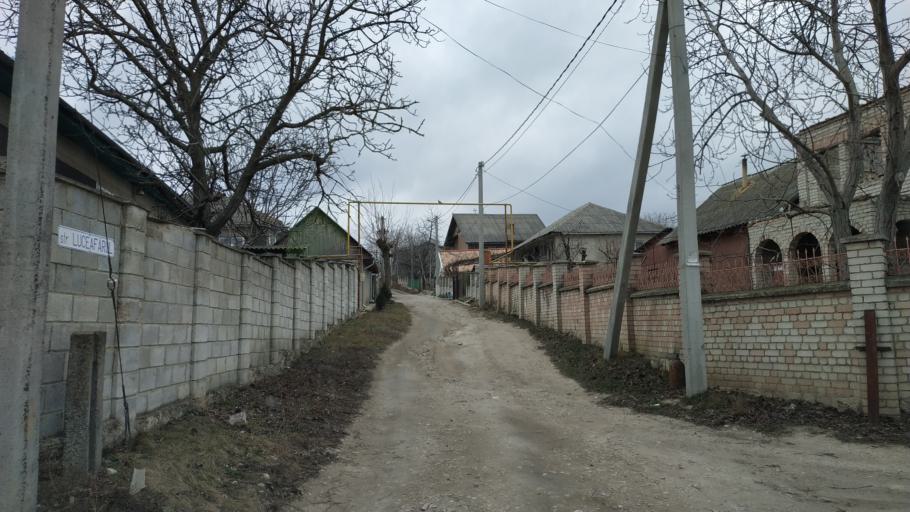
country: MD
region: Laloveni
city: Ialoveni
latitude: 46.9323
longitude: 28.7738
